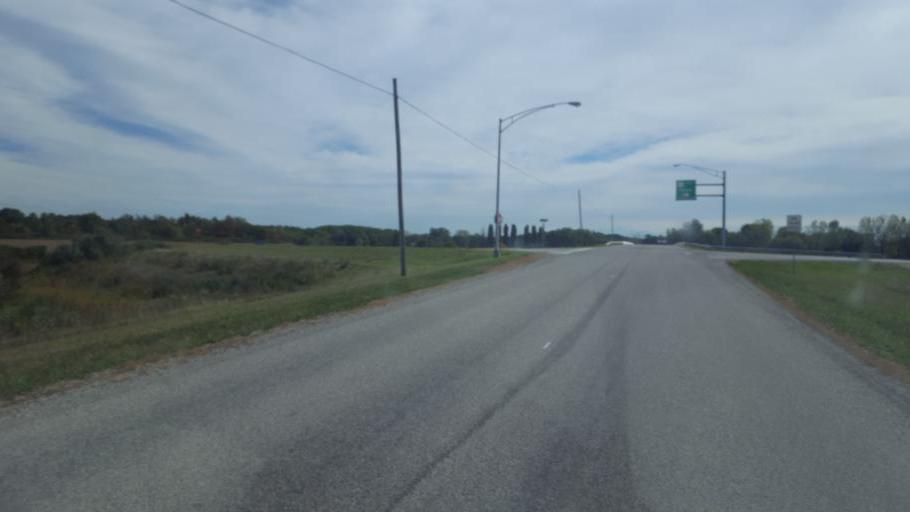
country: US
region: Ohio
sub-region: Erie County
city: Huron
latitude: 41.3696
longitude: -82.5228
